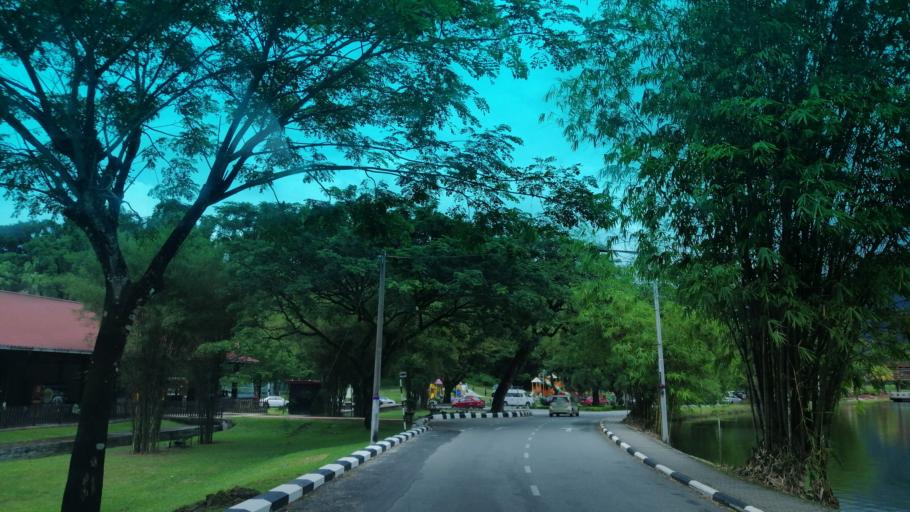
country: MY
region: Perak
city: Taiping
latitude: 4.8528
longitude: 100.7462
